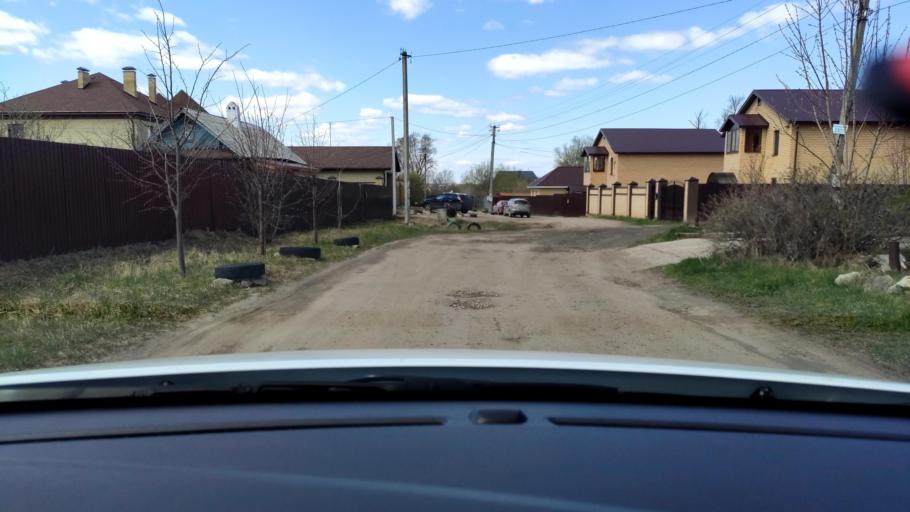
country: RU
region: Tatarstan
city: Stolbishchi
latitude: 55.7179
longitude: 49.3512
